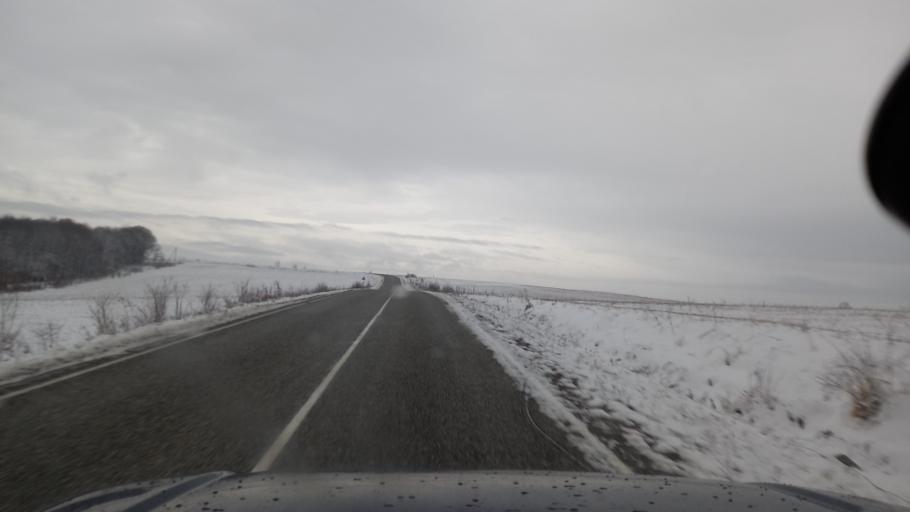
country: RU
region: Adygeya
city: Abadzekhskaya
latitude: 44.3417
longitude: 40.3519
